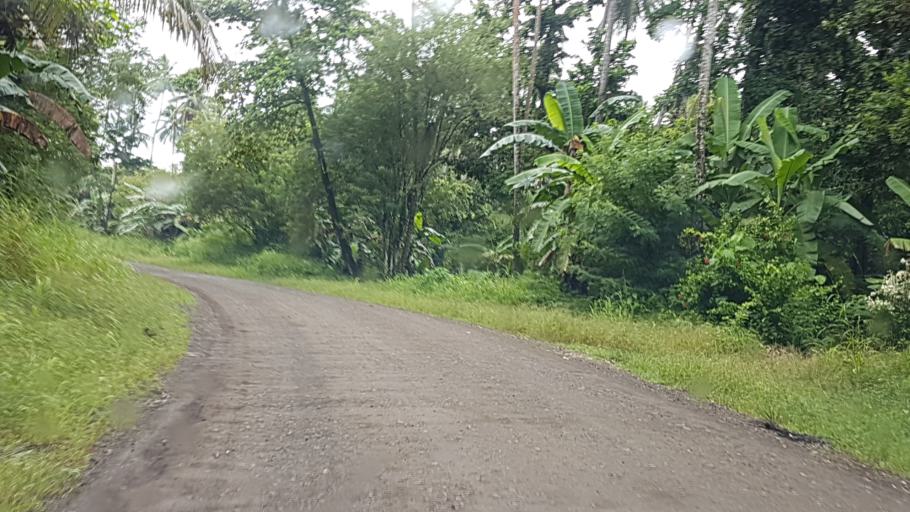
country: PG
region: Milne Bay
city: Alotau
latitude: -10.3392
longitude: 150.6236
